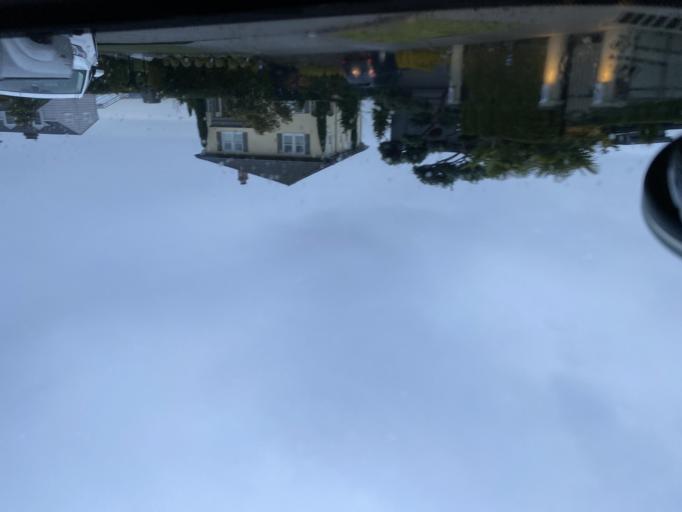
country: US
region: Washington
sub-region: King County
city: Seattle
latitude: 47.6411
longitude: -122.4057
